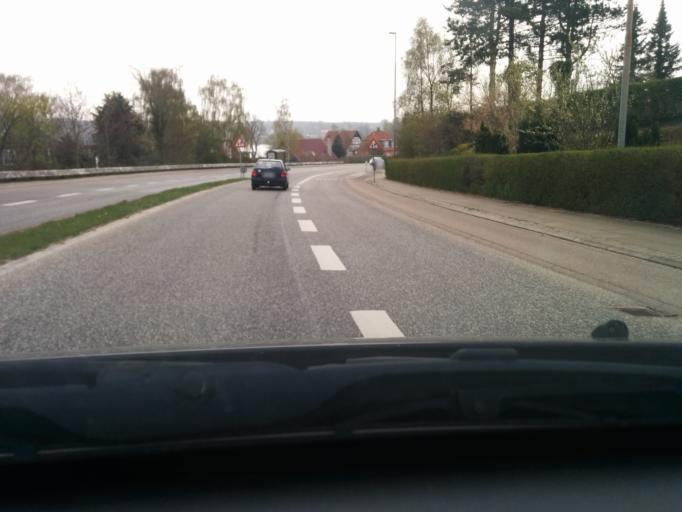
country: DK
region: Central Jutland
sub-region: Viborg Kommune
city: Viborg
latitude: 56.4555
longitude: 9.4147
